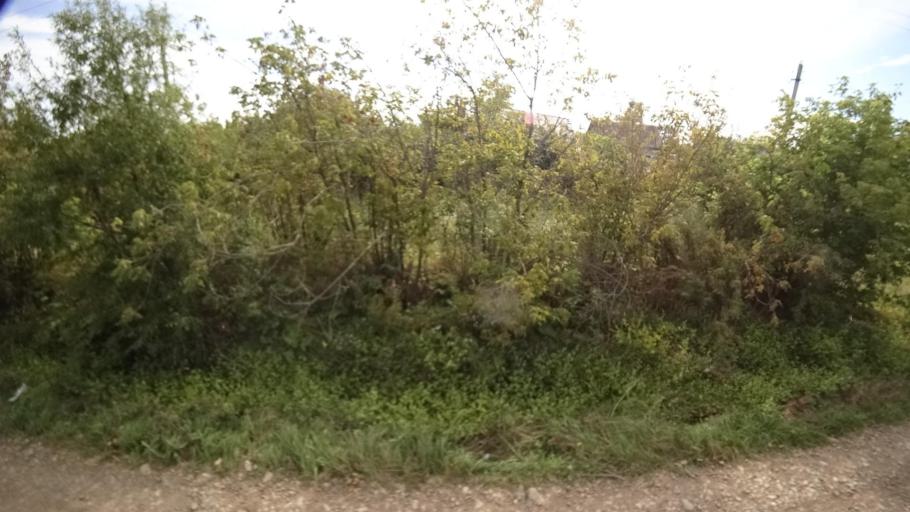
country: RU
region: Primorskiy
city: Dostoyevka
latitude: 44.3059
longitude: 133.4585
